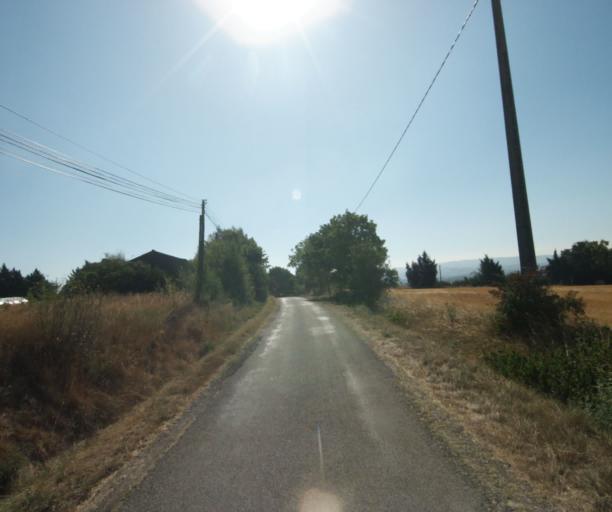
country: FR
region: Midi-Pyrenees
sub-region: Departement de la Haute-Garonne
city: Saint-Felix-Lauragais
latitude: 43.4934
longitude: 1.9266
